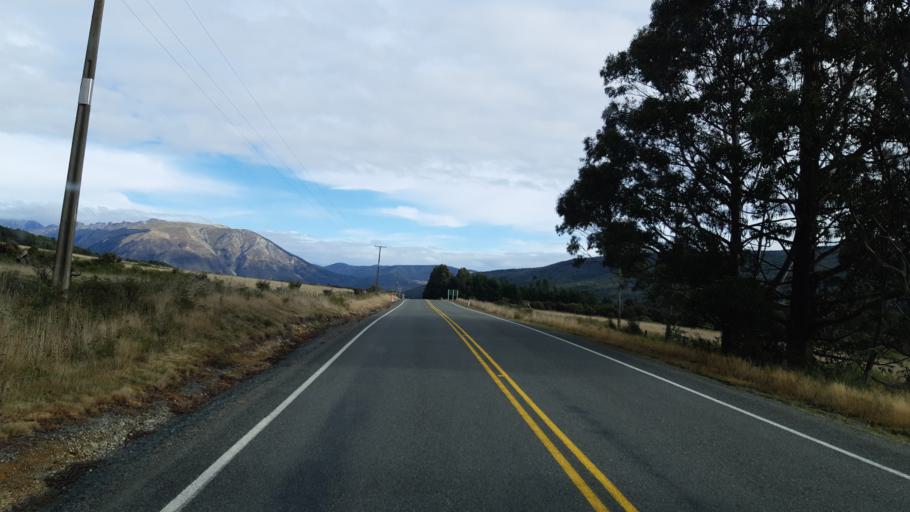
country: NZ
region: Tasman
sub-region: Tasman District
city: Wakefield
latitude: -41.7836
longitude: 172.8994
